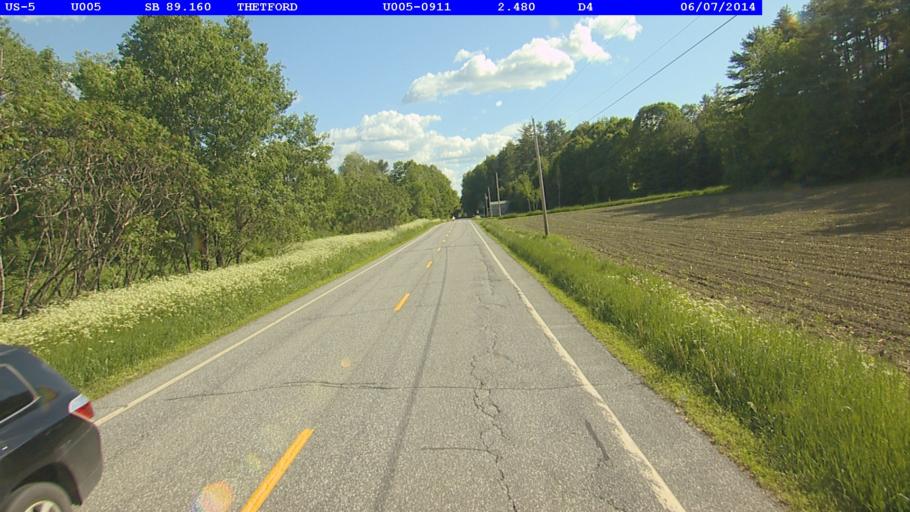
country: US
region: New Hampshire
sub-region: Grafton County
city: Lyme
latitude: 43.8046
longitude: -72.1915
